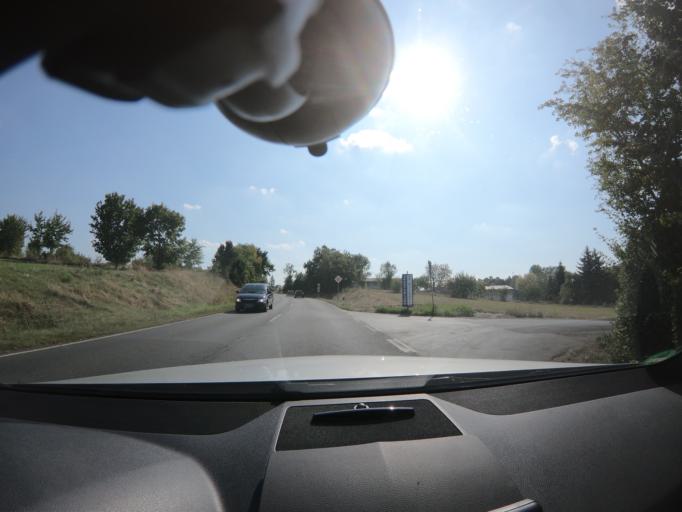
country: DE
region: Hesse
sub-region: Regierungsbezirk Giessen
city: Kirchhain
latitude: 50.8342
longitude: 8.9211
